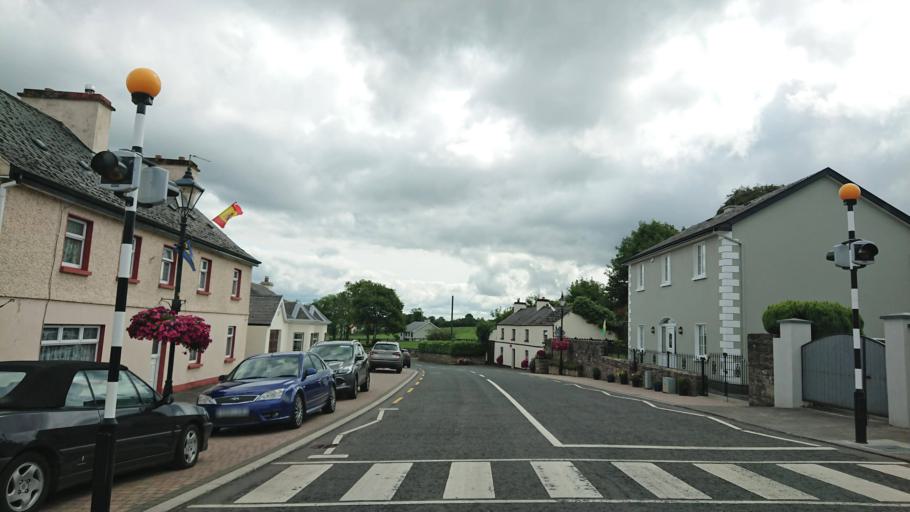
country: IE
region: Connaught
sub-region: County Leitrim
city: Carrick-on-Shannon
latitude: 54.0508
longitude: -8.1371
